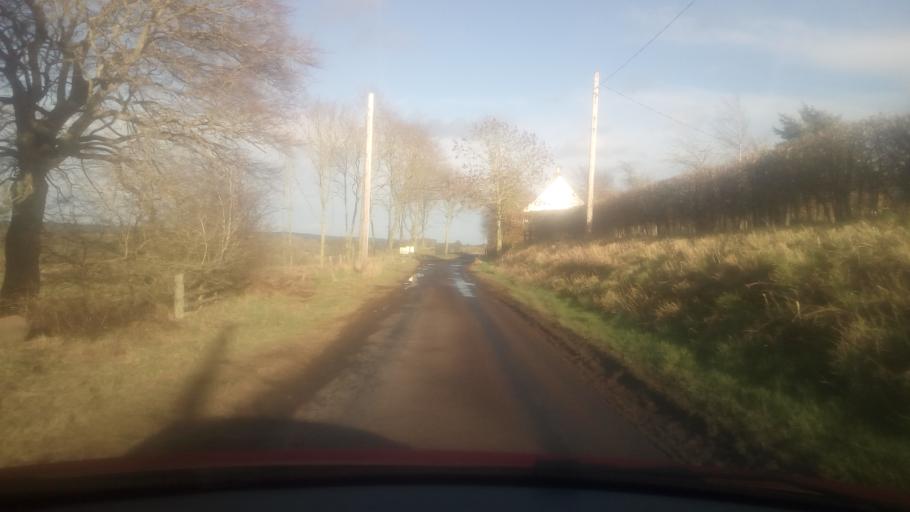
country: GB
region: Scotland
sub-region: The Scottish Borders
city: Duns
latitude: 55.7359
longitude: -2.3575
